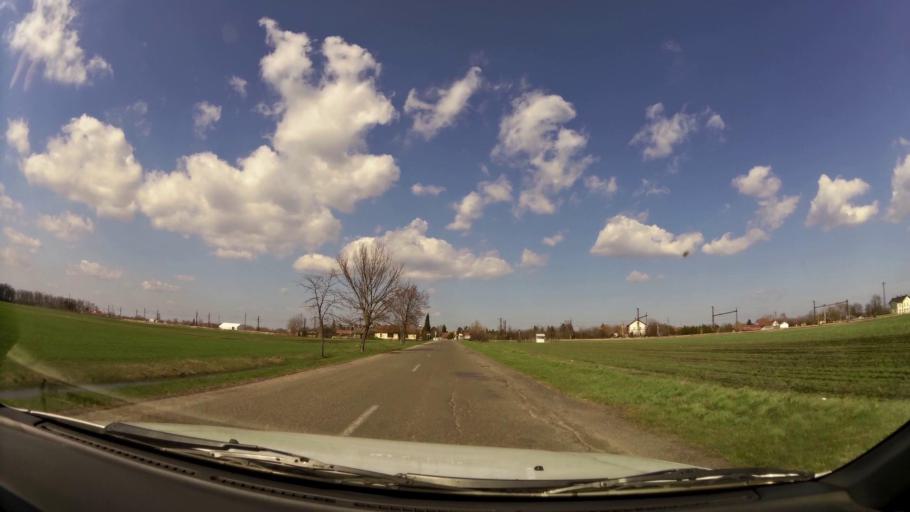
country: HU
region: Pest
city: Tapiogyorgye
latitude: 47.3238
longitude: 19.9463
